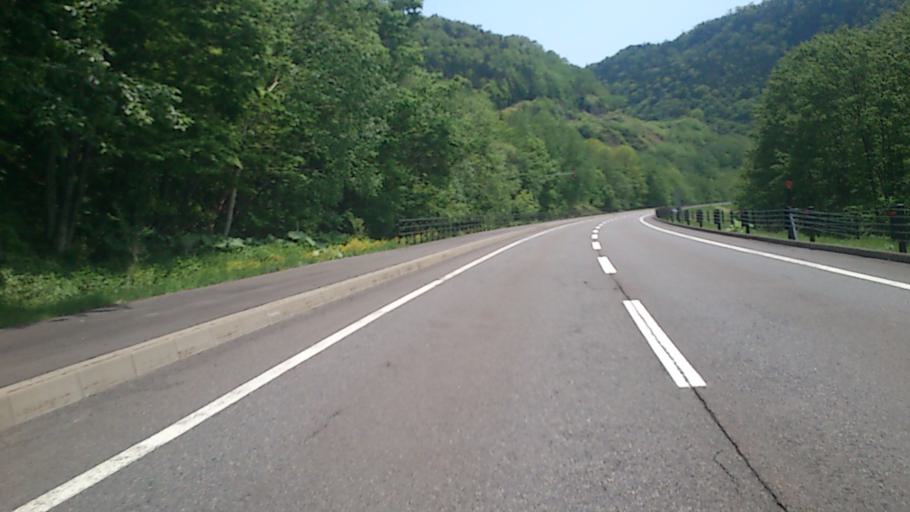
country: JP
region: Hokkaido
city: Otofuke
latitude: 43.3684
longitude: 143.2320
